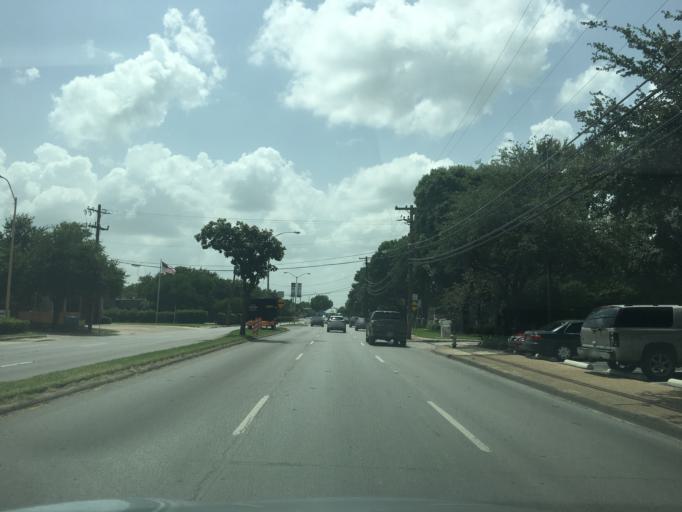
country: US
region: Texas
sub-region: Dallas County
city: University Park
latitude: 32.8949
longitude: -96.8056
